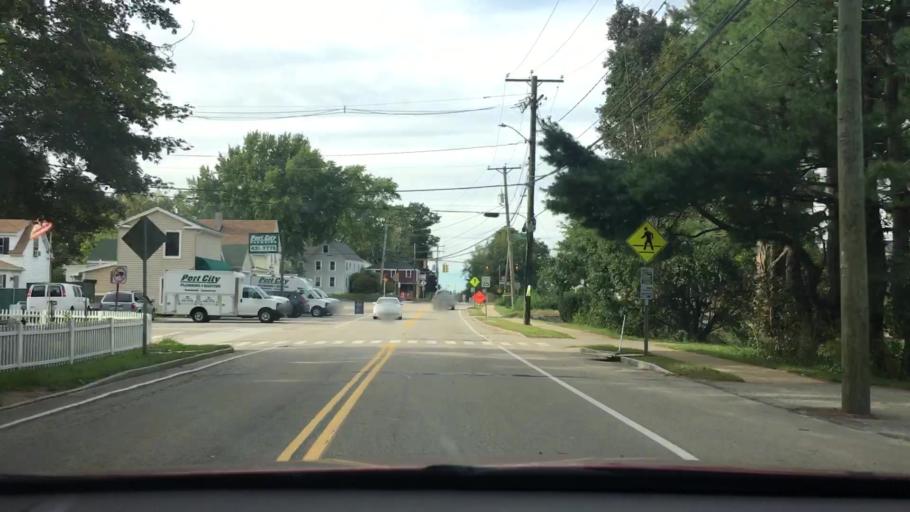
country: US
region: Maine
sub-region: York County
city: South Eliot
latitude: 43.0844
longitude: -70.7867
